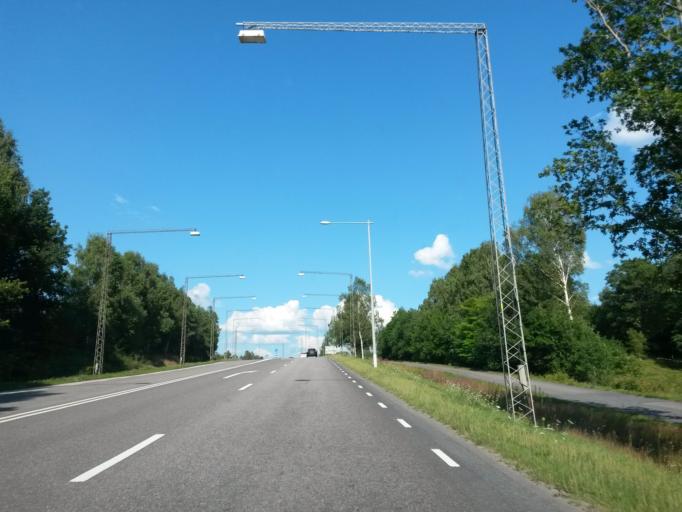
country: SE
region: Vaestra Goetaland
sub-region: Goteborg
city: Rannebergen
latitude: 57.7817
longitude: 12.0792
